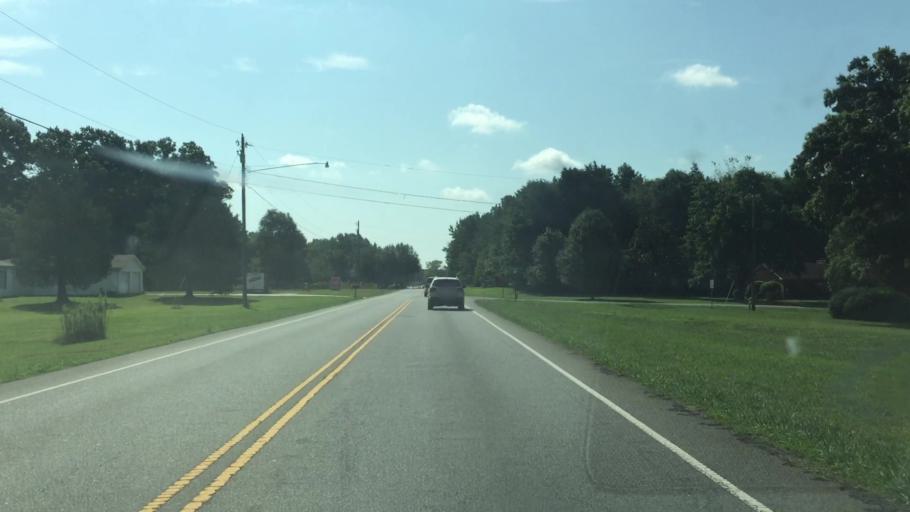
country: US
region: North Carolina
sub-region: Mecklenburg County
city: Mint Hill
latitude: 35.1750
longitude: -80.6222
